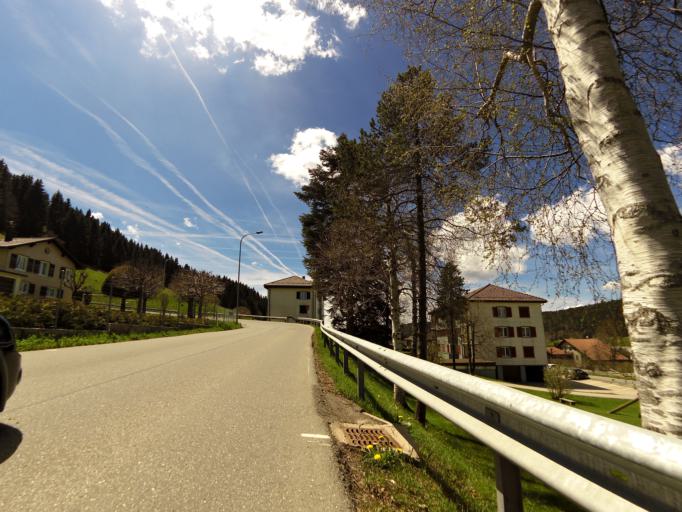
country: CH
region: Vaud
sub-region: Jura-Nord vaudois District
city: Le Chenit
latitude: 46.5784
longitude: 6.2055
